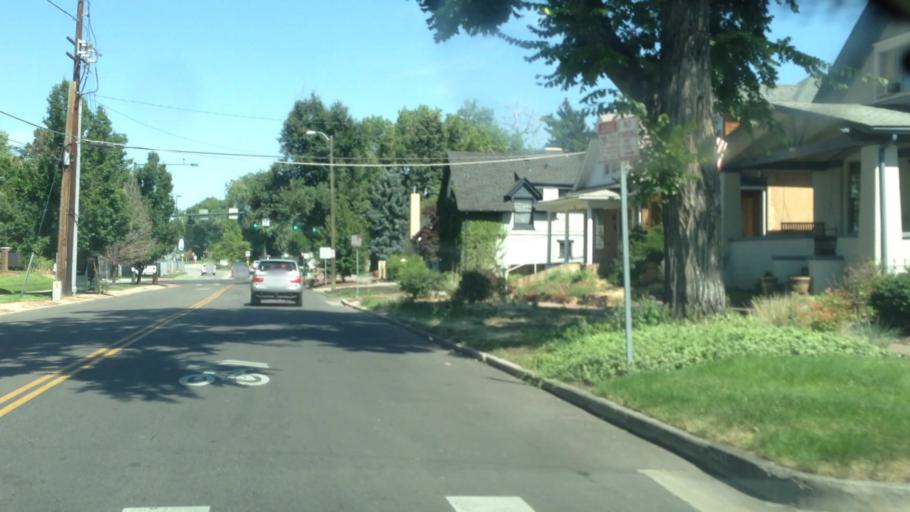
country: US
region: Colorado
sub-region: Denver County
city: Denver
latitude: 39.7507
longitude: -104.9609
